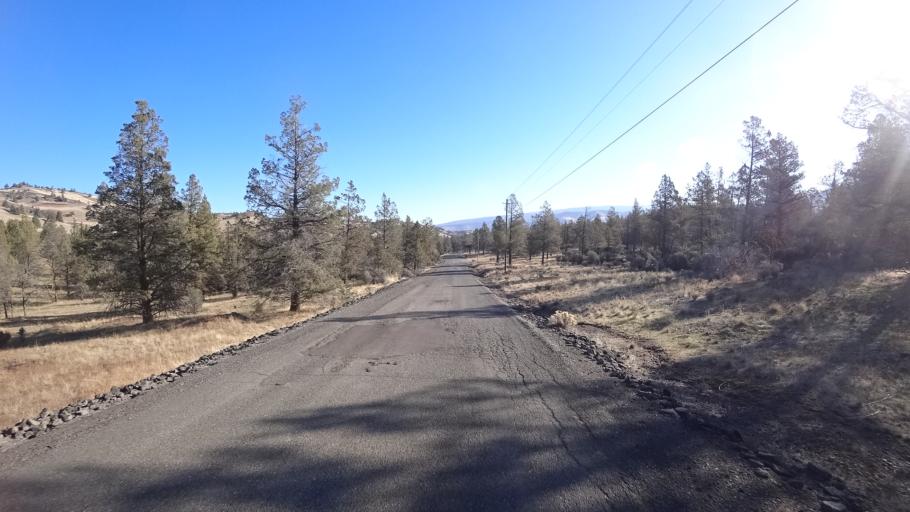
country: US
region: California
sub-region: Siskiyou County
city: Montague
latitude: 41.8895
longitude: -122.4393
